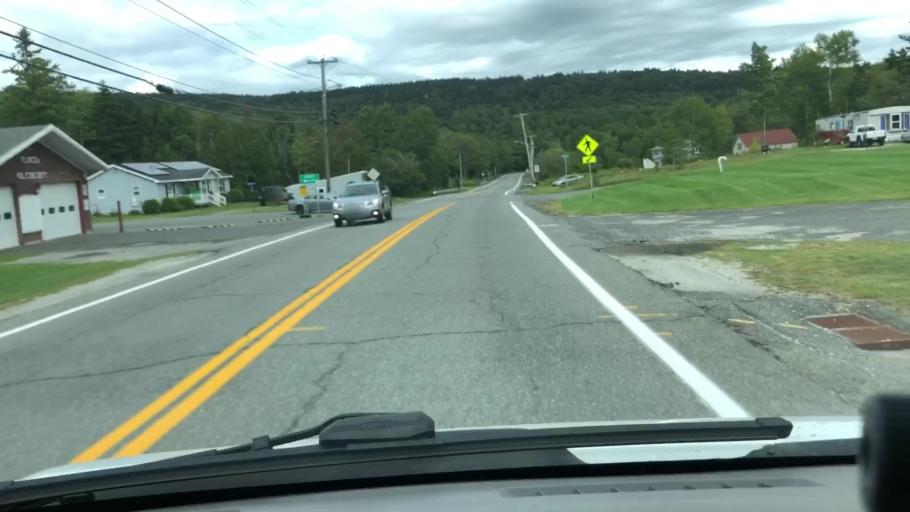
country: US
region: Massachusetts
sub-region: Berkshire County
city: North Adams
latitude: 42.6951
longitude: -73.0353
